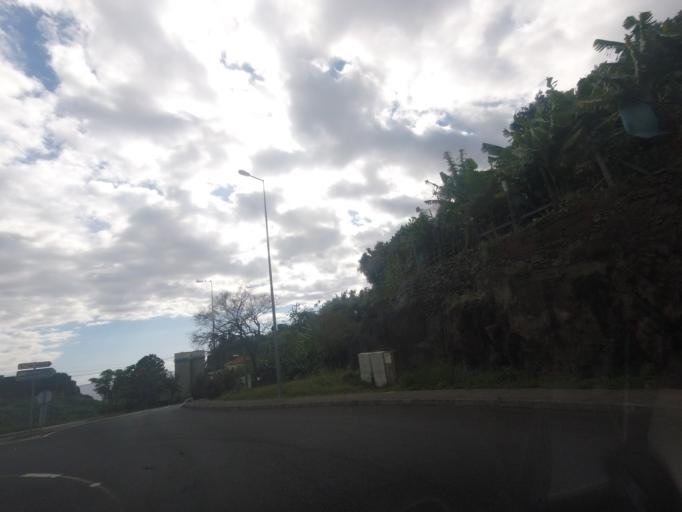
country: PT
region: Madeira
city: Camara de Lobos
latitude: 32.6475
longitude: -16.9664
